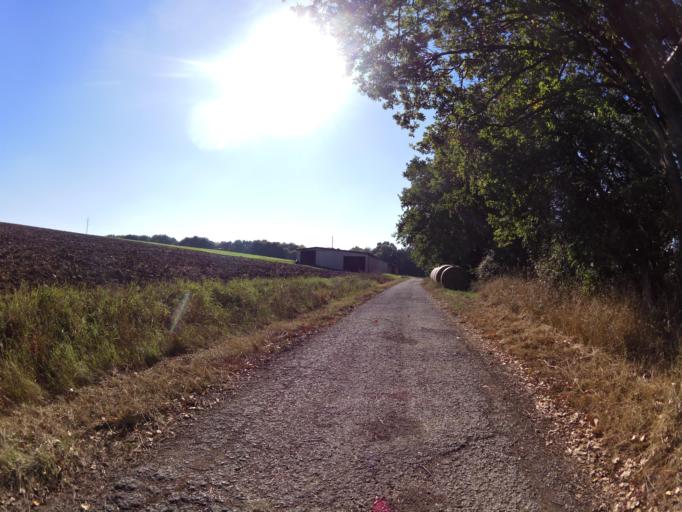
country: DE
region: Bavaria
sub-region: Regierungsbezirk Unterfranken
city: Ochsenfurt
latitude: 49.6800
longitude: 10.0506
